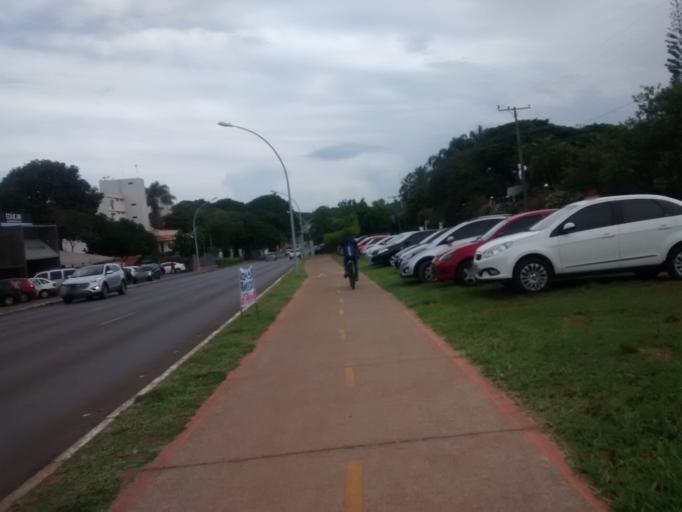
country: BR
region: Federal District
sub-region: Brasilia
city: Brasilia
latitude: -15.7541
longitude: -47.8972
